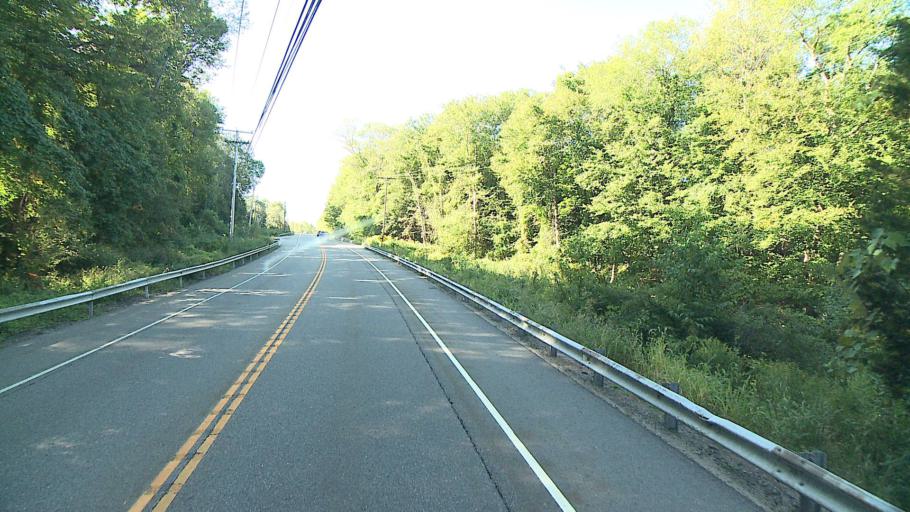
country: US
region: Connecticut
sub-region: New London County
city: Gales Ferry
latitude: 41.4394
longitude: -72.0801
